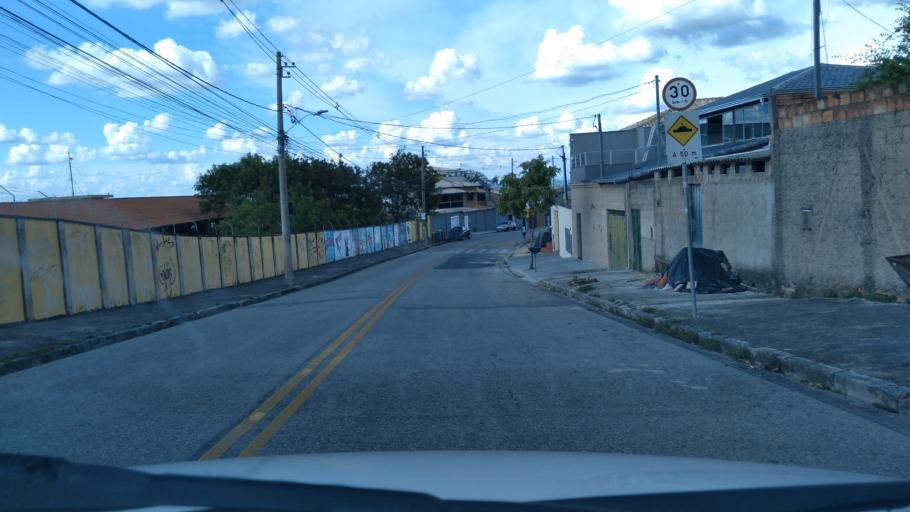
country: BR
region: Minas Gerais
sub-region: Belo Horizonte
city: Belo Horizonte
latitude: -19.8612
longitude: -43.8819
